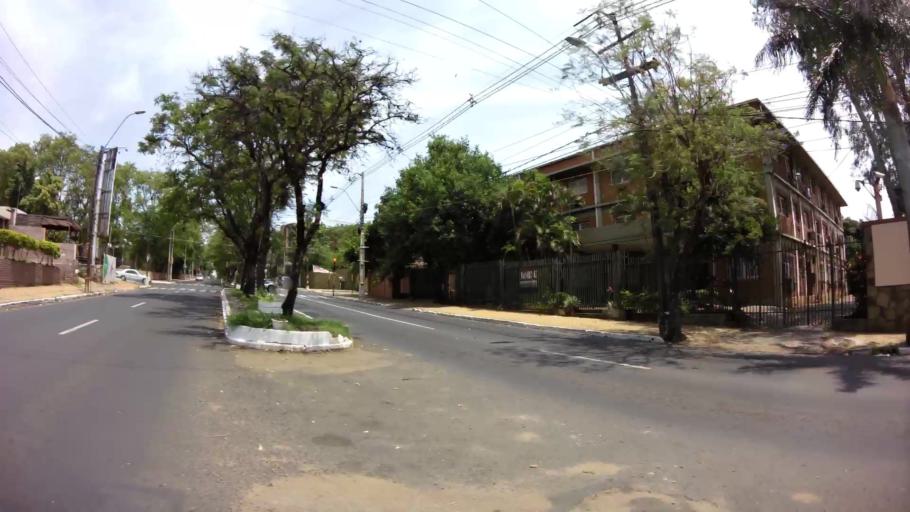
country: PY
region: Asuncion
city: Asuncion
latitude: -25.2976
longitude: -57.6047
